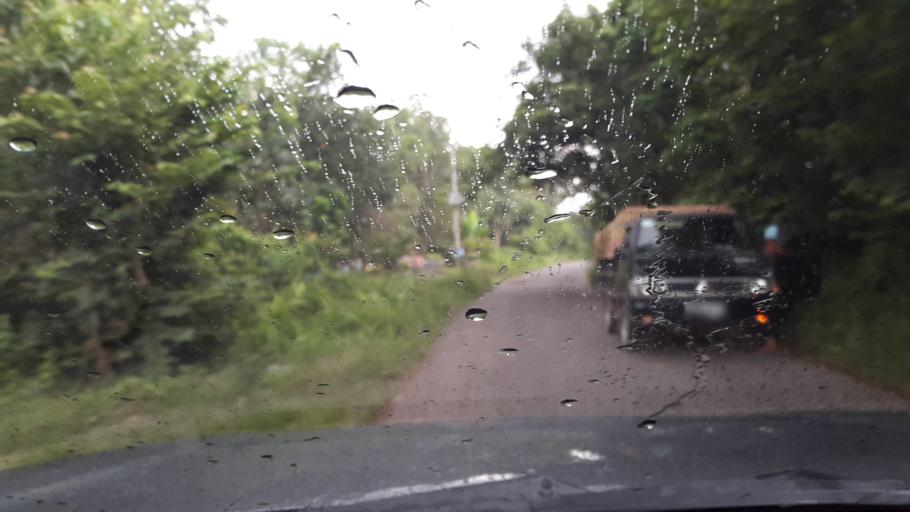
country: ID
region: South Sumatra
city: Sekayu
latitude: -2.9430
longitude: 103.7640
